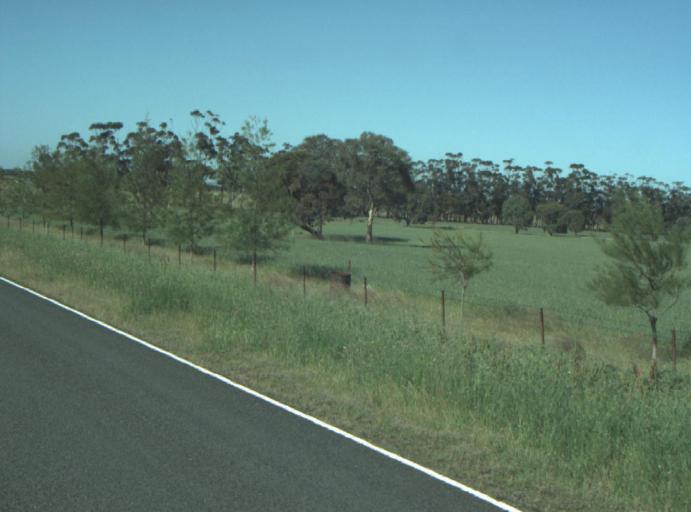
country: AU
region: Victoria
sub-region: Greater Geelong
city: Lara
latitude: -37.9700
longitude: 144.4058
